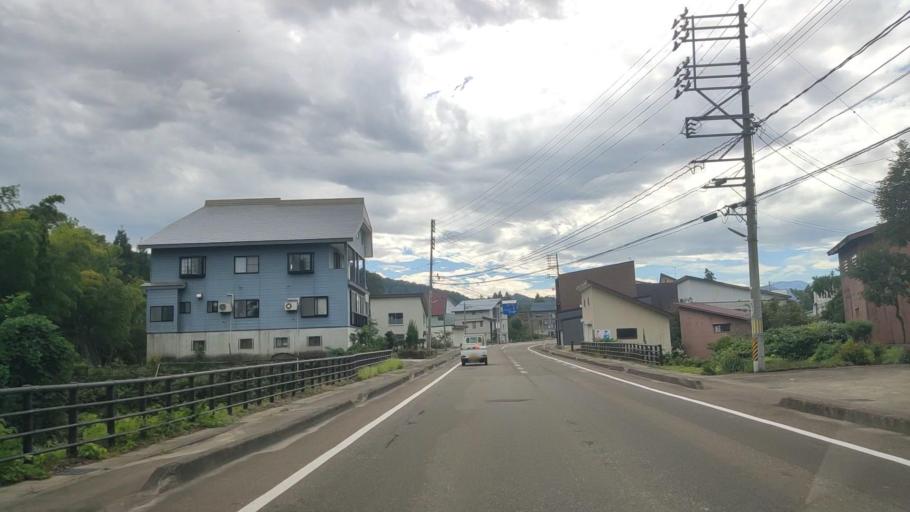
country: JP
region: Niigata
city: Arai
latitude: 36.9891
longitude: 138.2710
